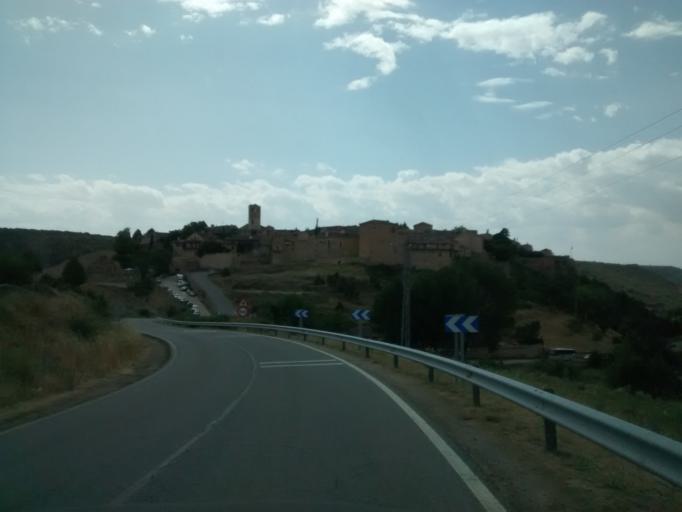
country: ES
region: Castille and Leon
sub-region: Provincia de Segovia
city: Pedraza
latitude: 41.1310
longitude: -3.8063
